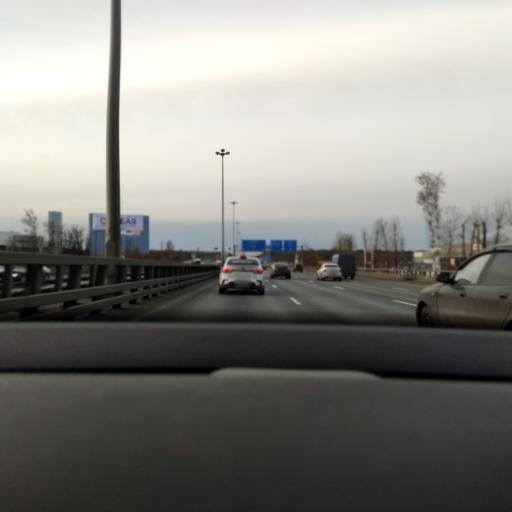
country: RU
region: Moscow
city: Solntsevo
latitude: 55.6204
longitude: 37.3951
